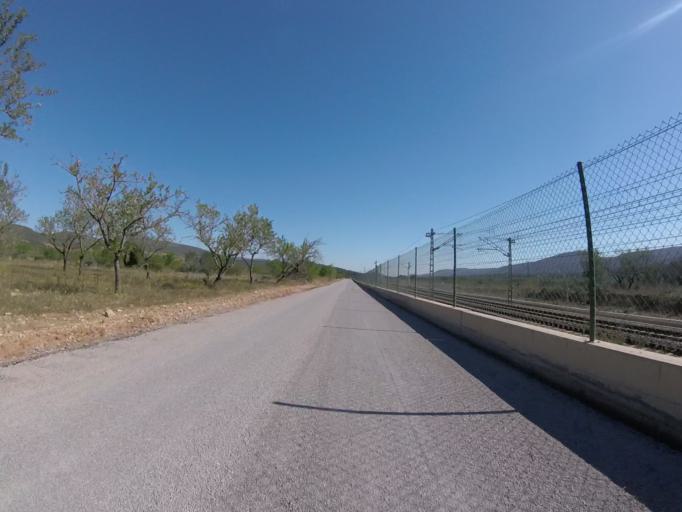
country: ES
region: Valencia
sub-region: Provincia de Castello
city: Alcala de Xivert
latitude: 40.3363
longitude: 0.2554
